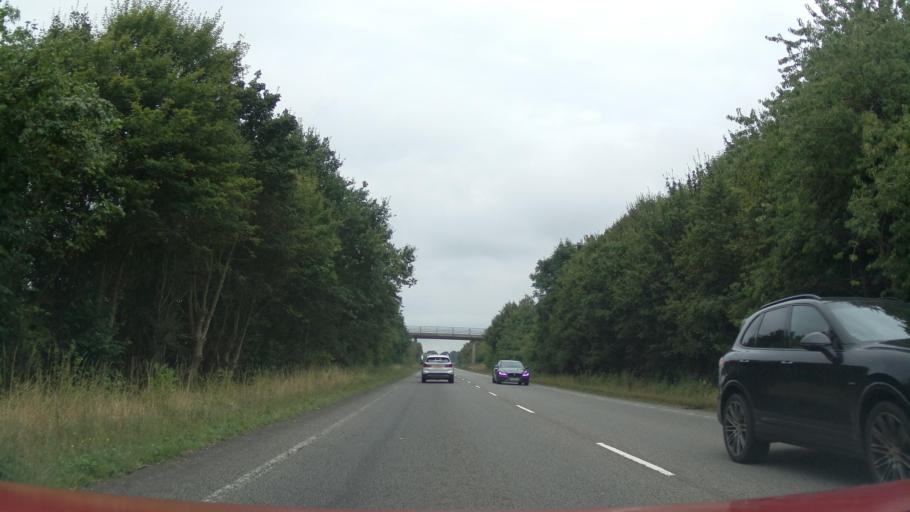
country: GB
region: England
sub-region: Nottinghamshire
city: South Collingham
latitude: 53.0919
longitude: -0.7677
